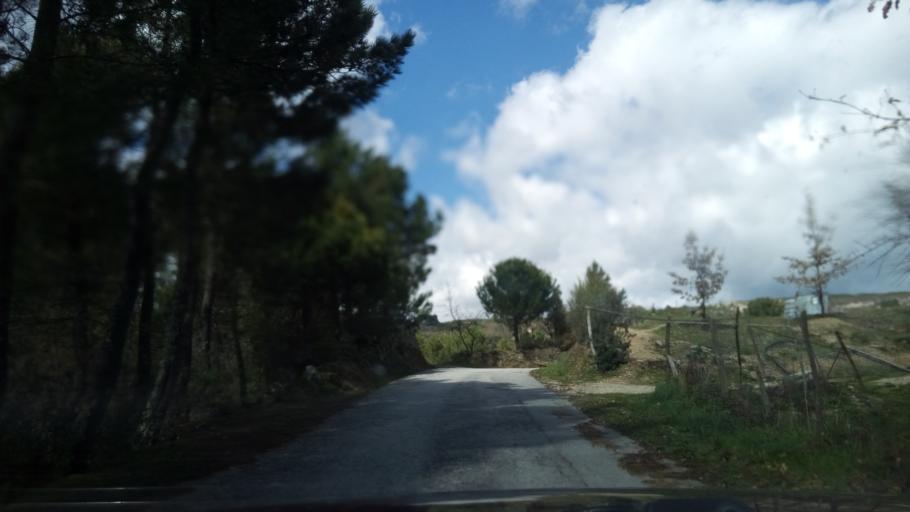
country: PT
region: Guarda
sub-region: Fornos de Algodres
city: Fornos de Algodres
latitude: 40.6289
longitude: -7.5259
